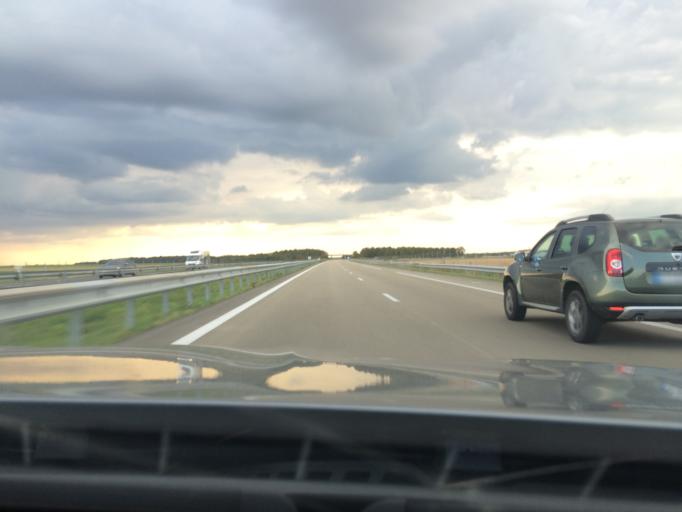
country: FR
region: Ile-de-France
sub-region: Departement de Seine-et-Marne
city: Egreville
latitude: 48.1916
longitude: 2.8166
